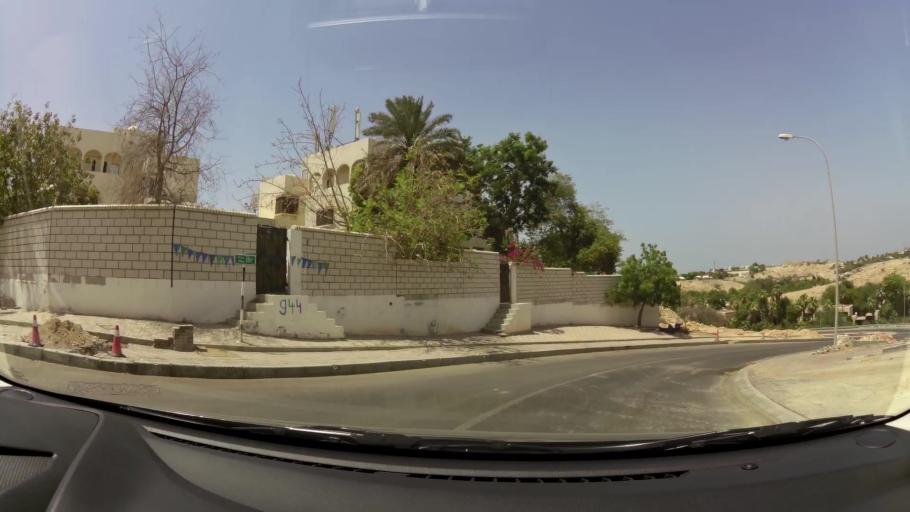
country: OM
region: Muhafazat Masqat
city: Muscat
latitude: 23.6318
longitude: 58.4872
